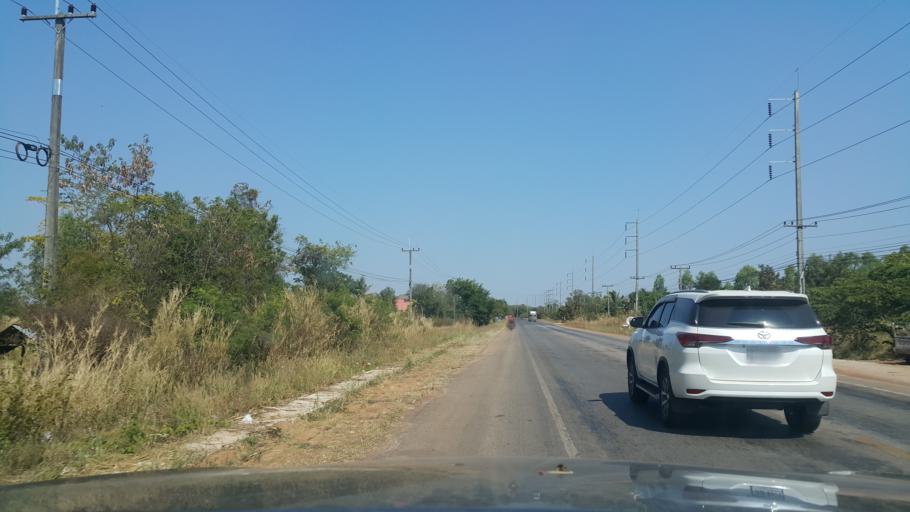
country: TH
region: Changwat Udon Thani
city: Thung Fon
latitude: 17.4950
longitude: 103.2007
